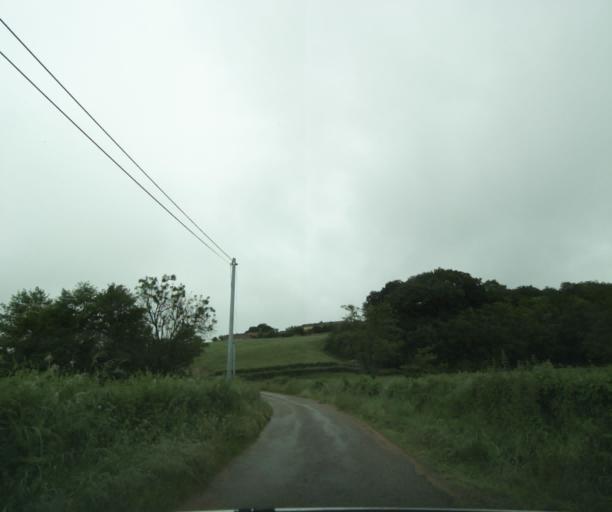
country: FR
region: Bourgogne
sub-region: Departement de Saone-et-Loire
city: Charolles
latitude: 46.4581
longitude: 4.3938
